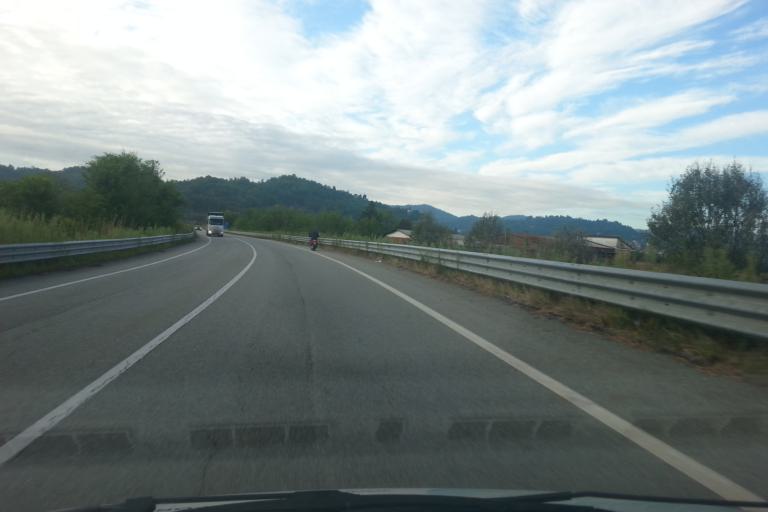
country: IT
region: Piedmont
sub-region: Provincia di Torino
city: San Raffaele Cimena
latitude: 45.1467
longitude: 7.8379
